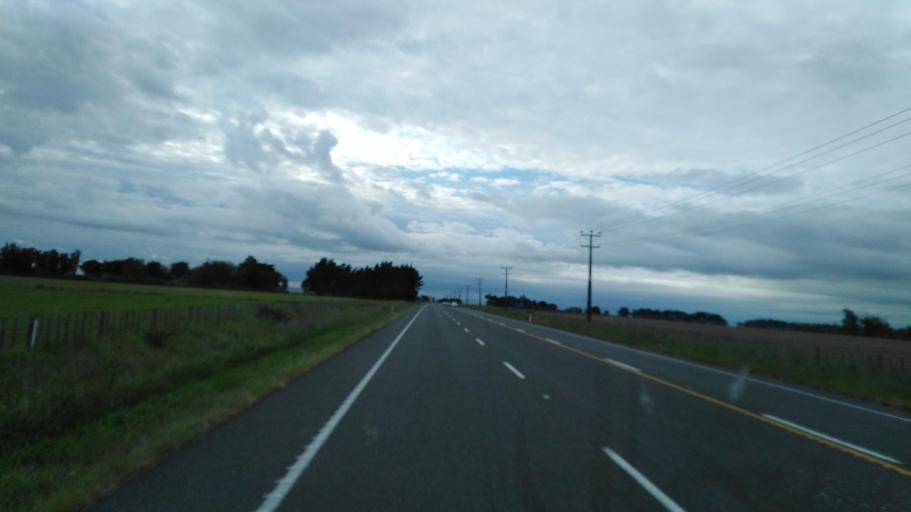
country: NZ
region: Manawatu-Wanganui
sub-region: Rangitikei District
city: Bulls
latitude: -40.1282
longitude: 175.3570
